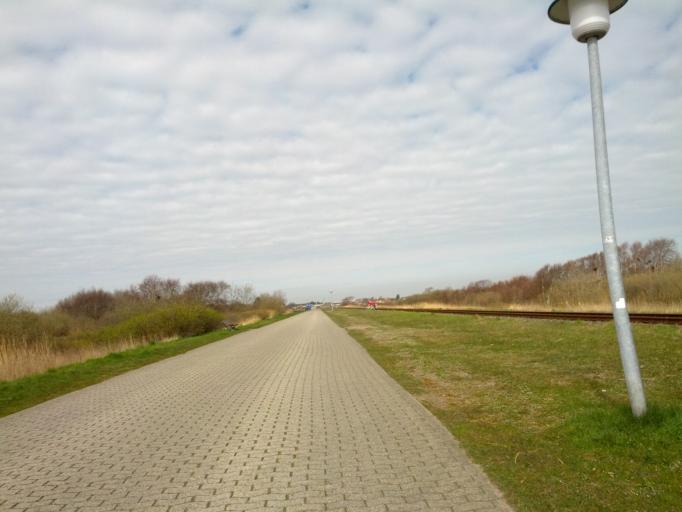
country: DE
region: Lower Saxony
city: Langeoog
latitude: 53.7383
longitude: 7.4908
